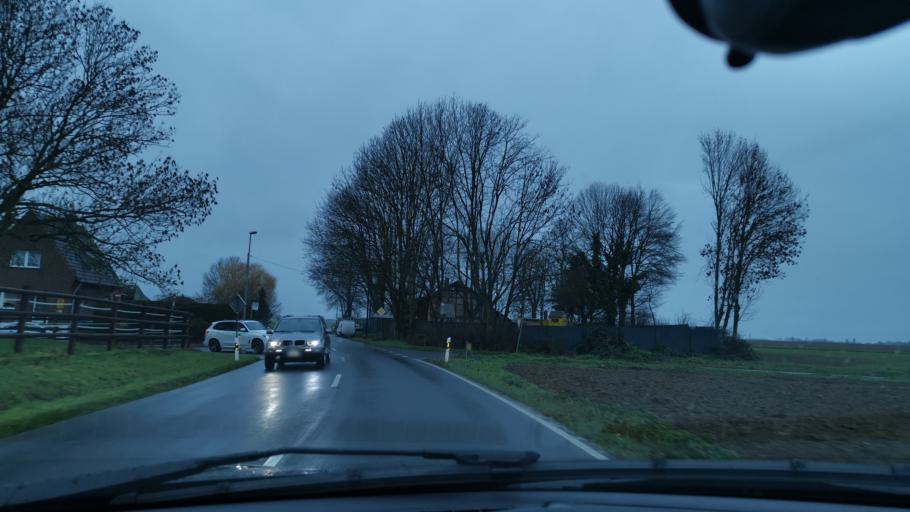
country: DE
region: North Rhine-Westphalia
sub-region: Regierungsbezirk Koln
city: Bedburg
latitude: 50.9985
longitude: 6.5147
